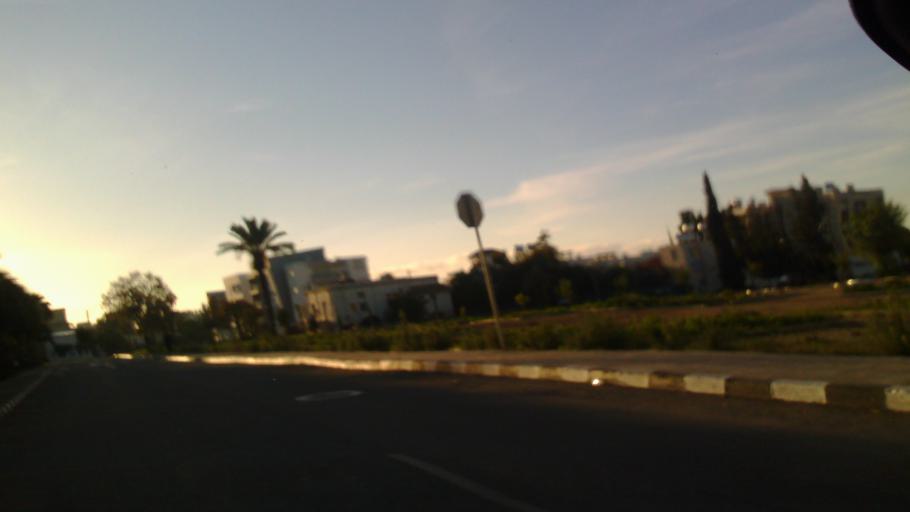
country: CY
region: Pafos
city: Paphos
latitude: 34.7791
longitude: 32.4269
